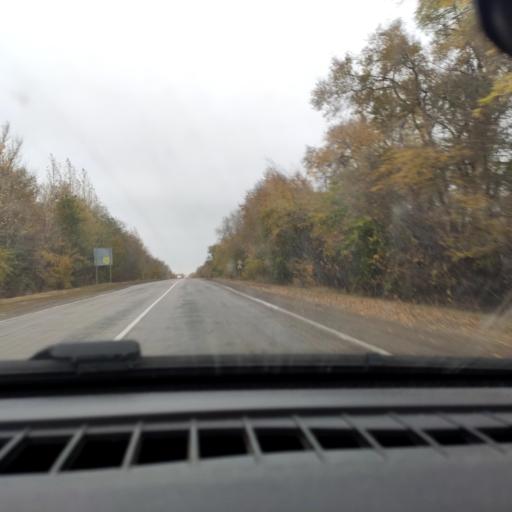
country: RU
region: Voronezj
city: Uryv-Pokrovka
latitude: 51.1447
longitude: 39.0577
